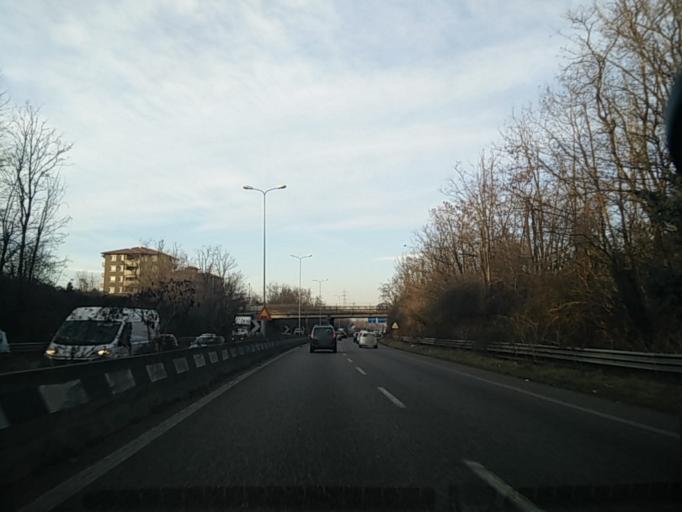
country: IT
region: Lombardy
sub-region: Provincia di Monza e Brianza
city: Varedo
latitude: 45.6084
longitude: 9.1659
